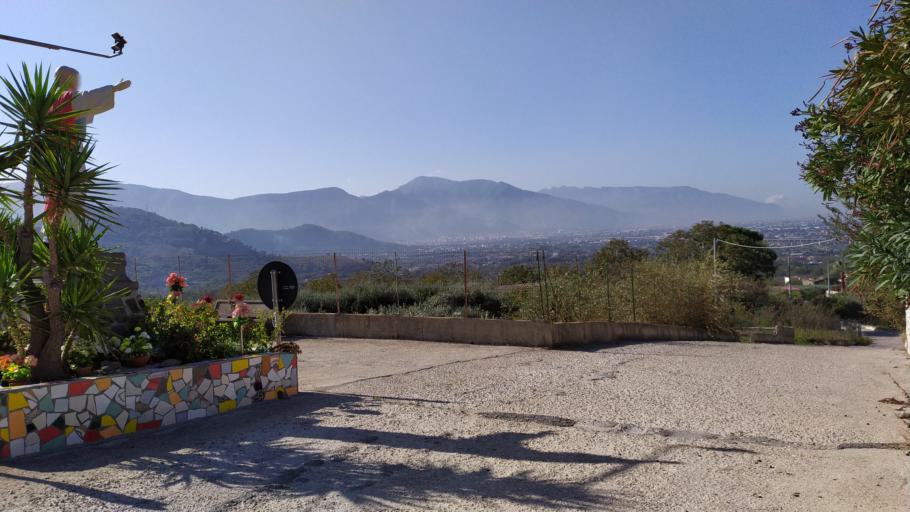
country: IT
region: Campania
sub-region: Provincia di Salerno
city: Sarno
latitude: 40.8049
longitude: 14.6566
